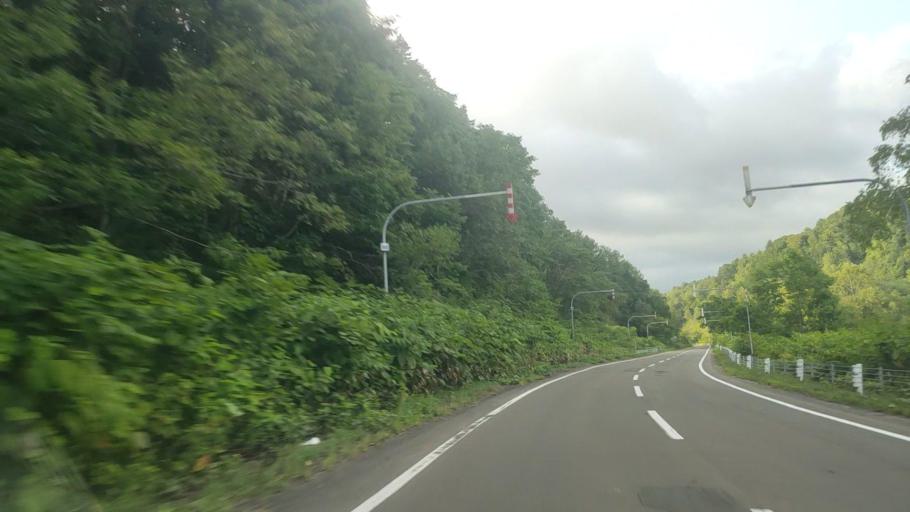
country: JP
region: Hokkaido
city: Bibai
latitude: 43.1346
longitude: 142.0946
